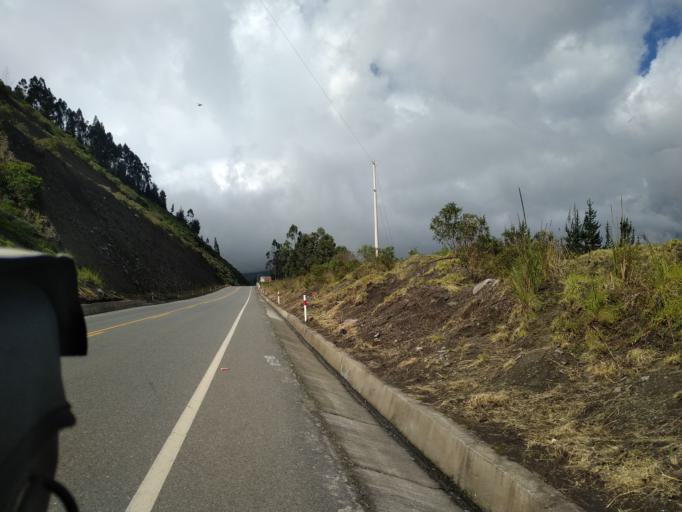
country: EC
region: Tungurahua
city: Banos
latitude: -1.4947
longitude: -78.5224
